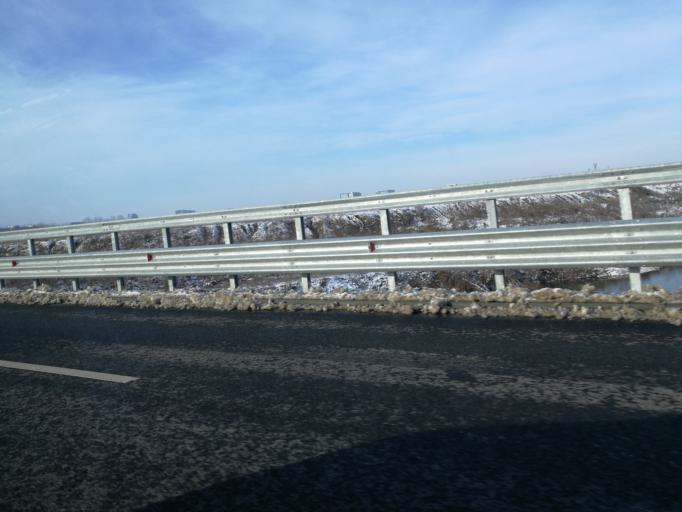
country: RO
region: Ilfov
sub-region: Comuna Fundeni-Dobroesti
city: Fundeni
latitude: 44.4785
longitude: 26.1342
